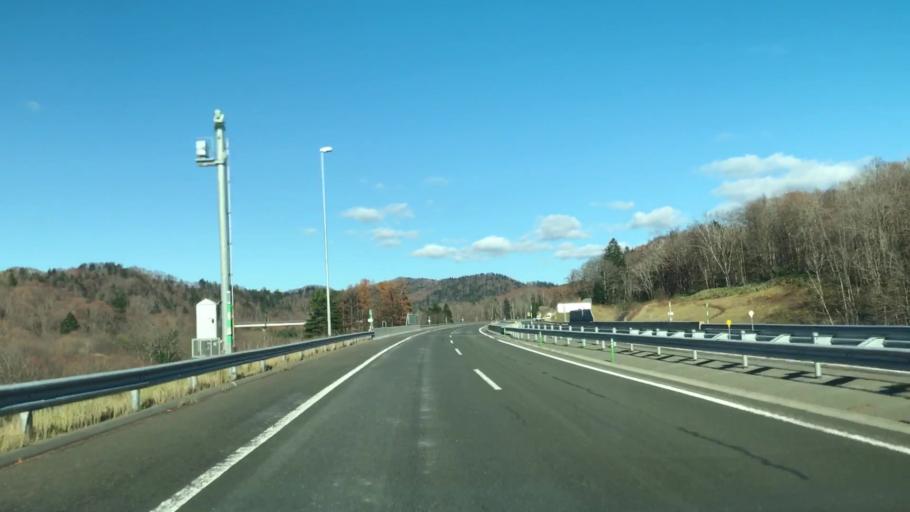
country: JP
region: Hokkaido
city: Shimo-furano
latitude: 42.9344
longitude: 142.2061
